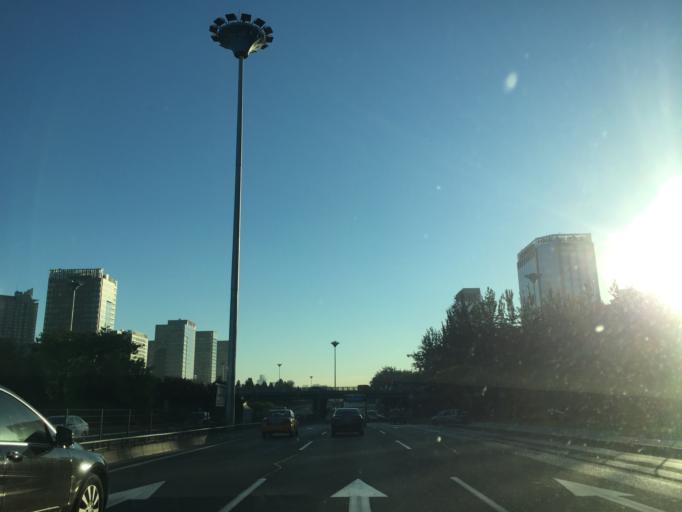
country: CN
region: Beijing
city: Chaowai
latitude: 39.9553
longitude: 116.4473
